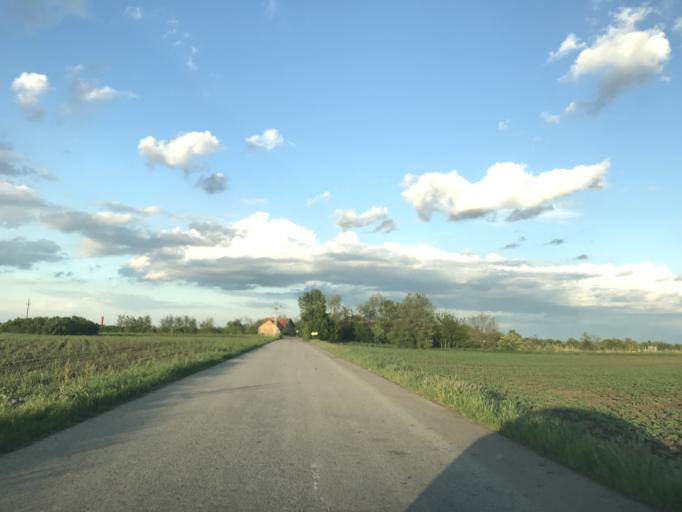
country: RS
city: Banatski Dvor
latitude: 45.5215
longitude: 20.4943
